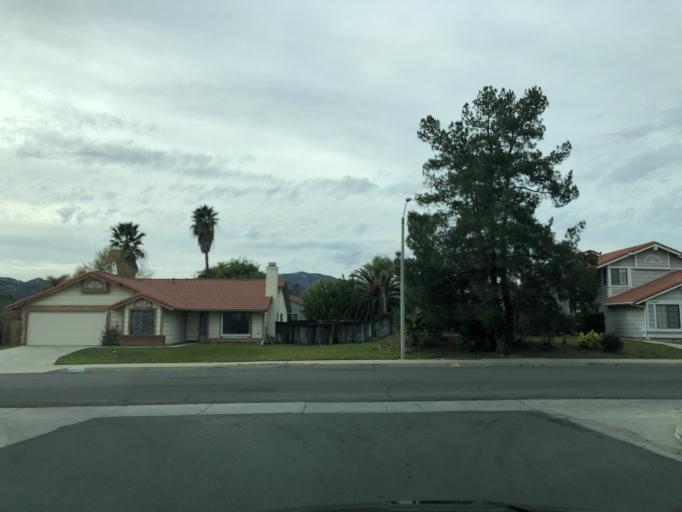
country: US
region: California
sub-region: Riverside County
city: Wildomar
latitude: 33.6059
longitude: -117.2619
